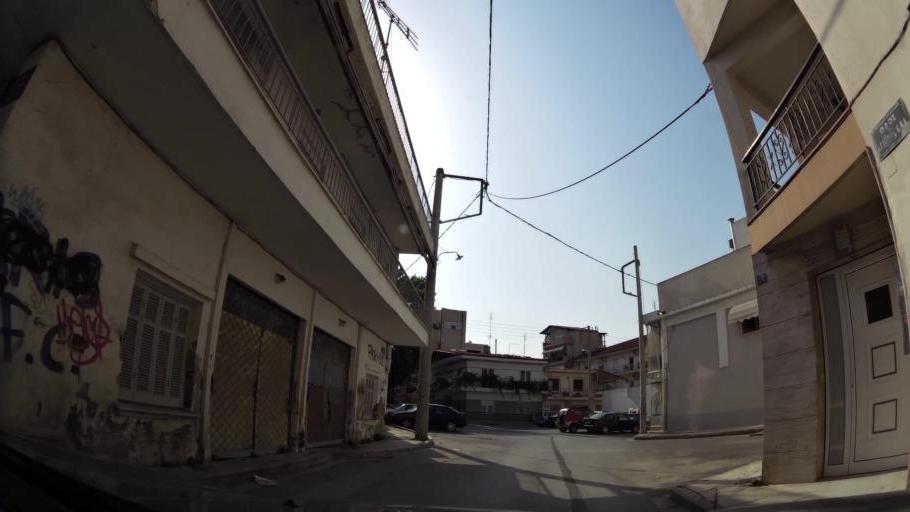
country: GR
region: Central Macedonia
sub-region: Nomos Thessalonikis
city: Evosmos
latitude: 40.6658
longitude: 22.9182
